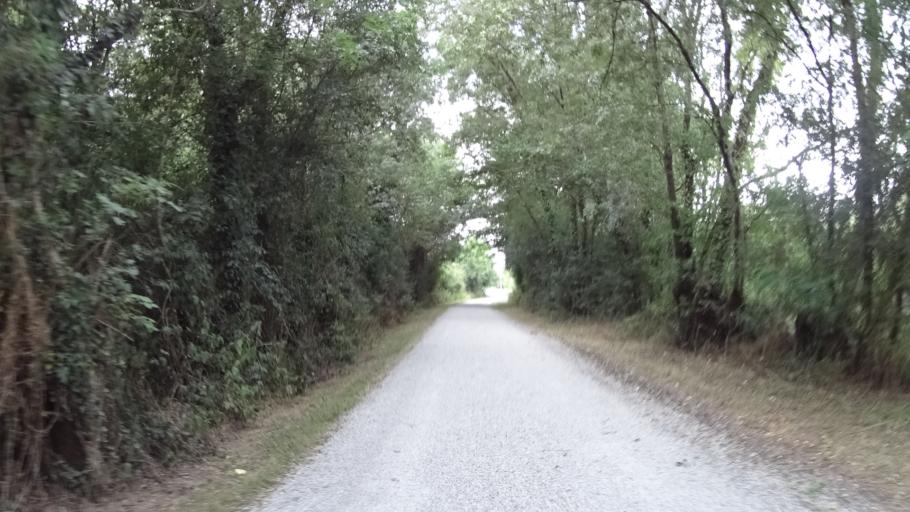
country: FR
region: Pays de la Loire
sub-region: Departement de la Loire-Atlantique
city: Oudon
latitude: 47.3423
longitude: -1.3015
